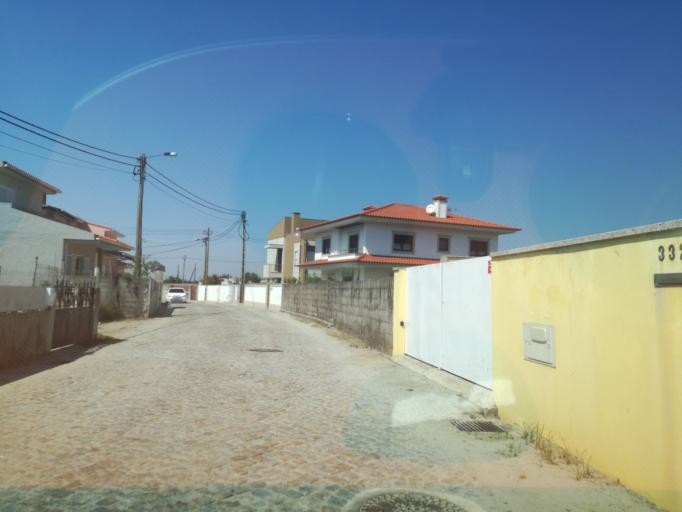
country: PT
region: Braga
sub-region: Esposende
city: Apulia
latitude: 41.4544
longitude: -8.7433
